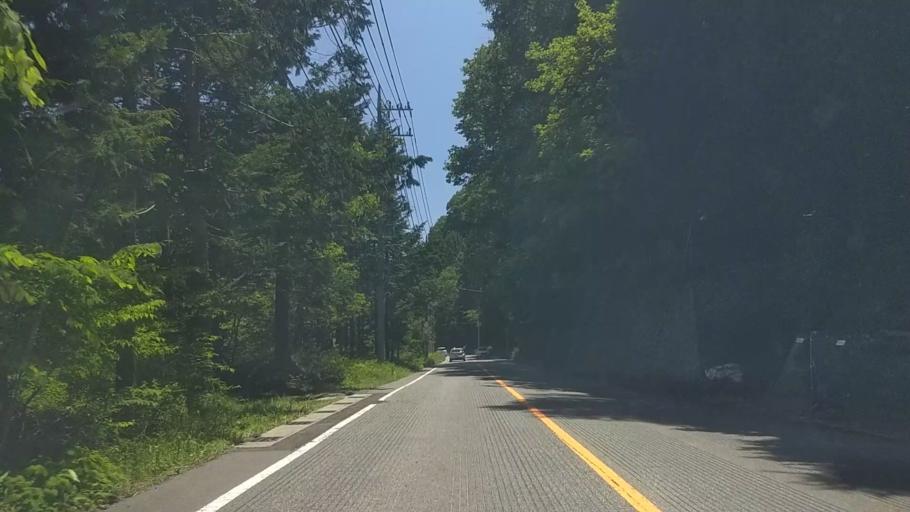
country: JP
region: Yamanashi
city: Nirasaki
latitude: 35.8813
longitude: 138.4266
